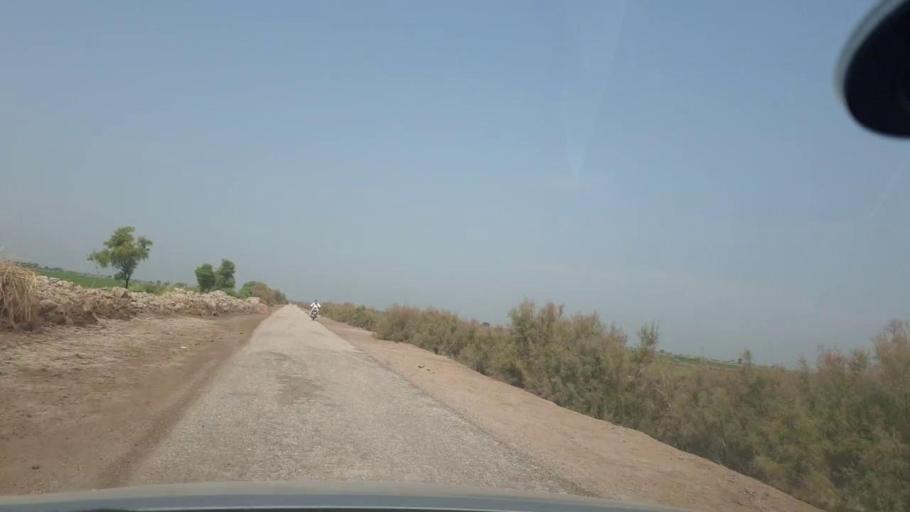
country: PK
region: Balochistan
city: Mehrabpur
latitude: 28.0585
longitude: 68.0732
